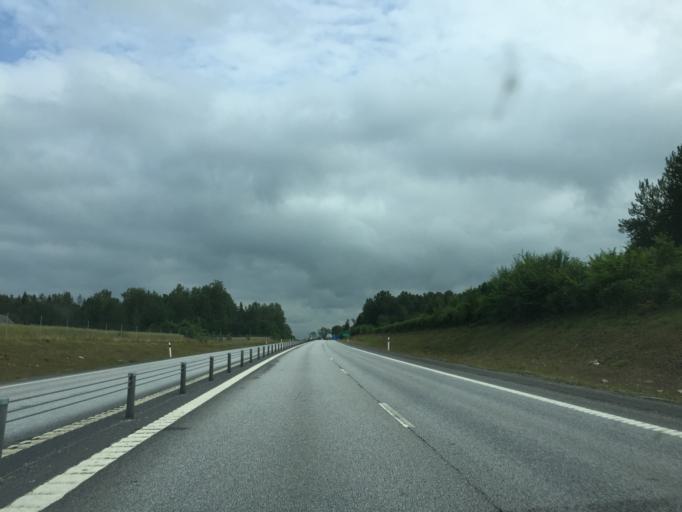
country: SE
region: OErebro
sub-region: Orebro Kommun
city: Vintrosa
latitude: 59.2510
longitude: 14.9198
